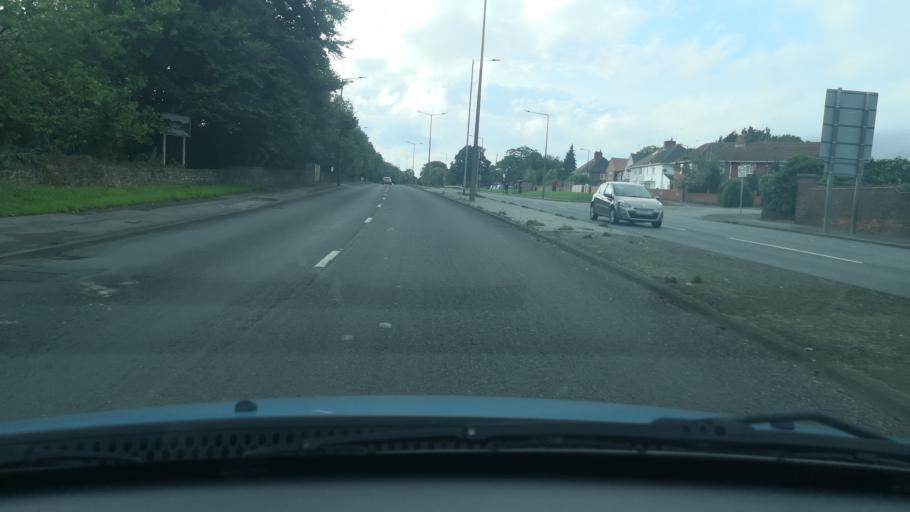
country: GB
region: England
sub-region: Doncaster
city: Carcroft
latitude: 53.5577
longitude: -1.1826
